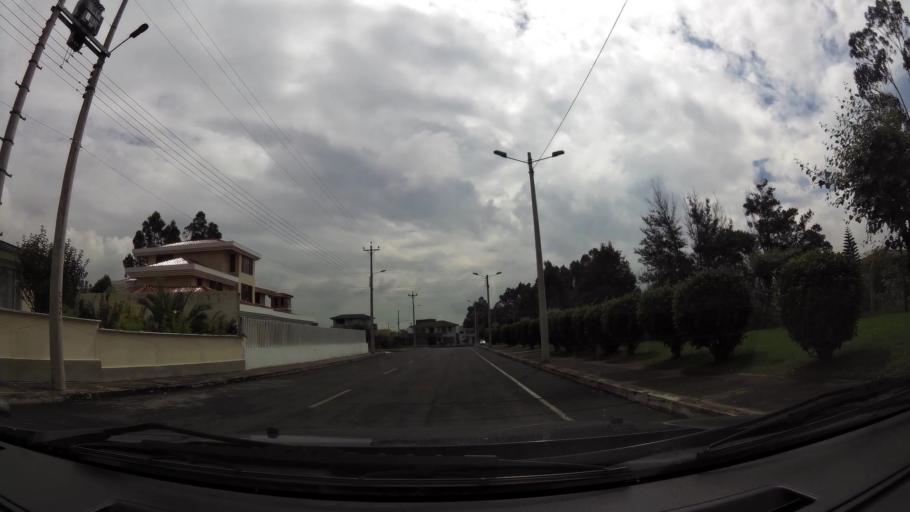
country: EC
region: Pichincha
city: Sangolqui
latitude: -0.3086
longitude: -78.4733
